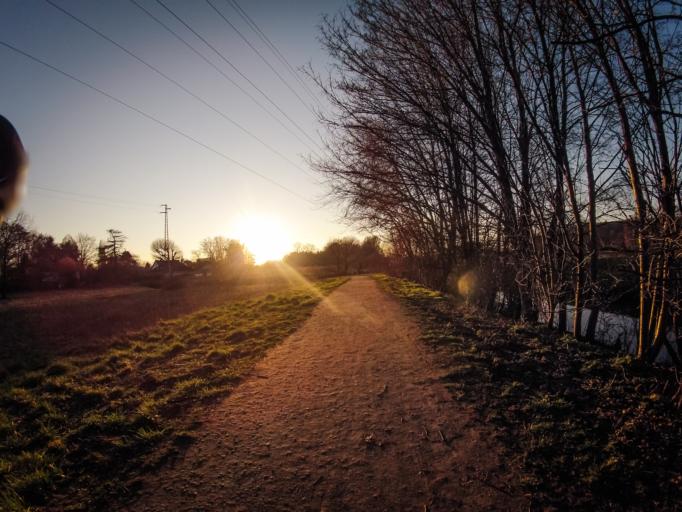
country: DE
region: Lower Saxony
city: Wallenhorst
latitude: 52.3102
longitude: 7.9923
